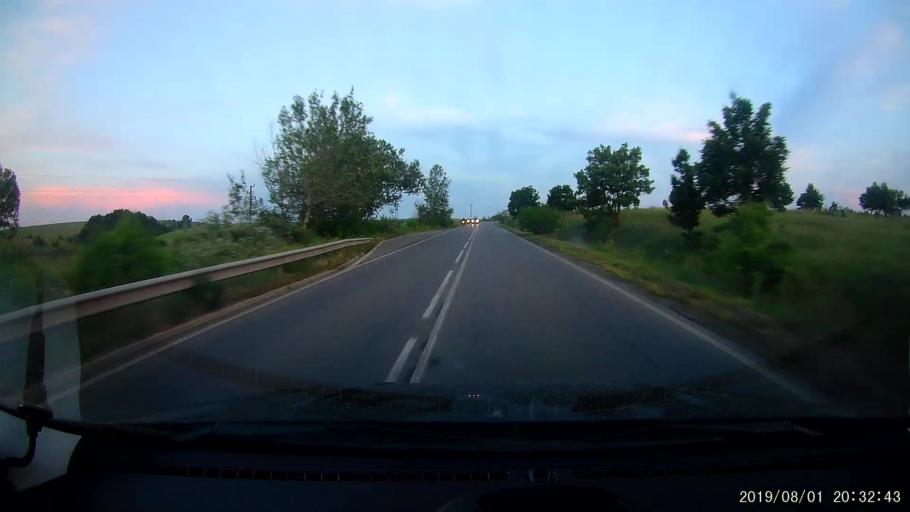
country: BG
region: Yambol
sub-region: Obshtina Elkhovo
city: Elkhovo
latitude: 42.1178
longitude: 26.5305
